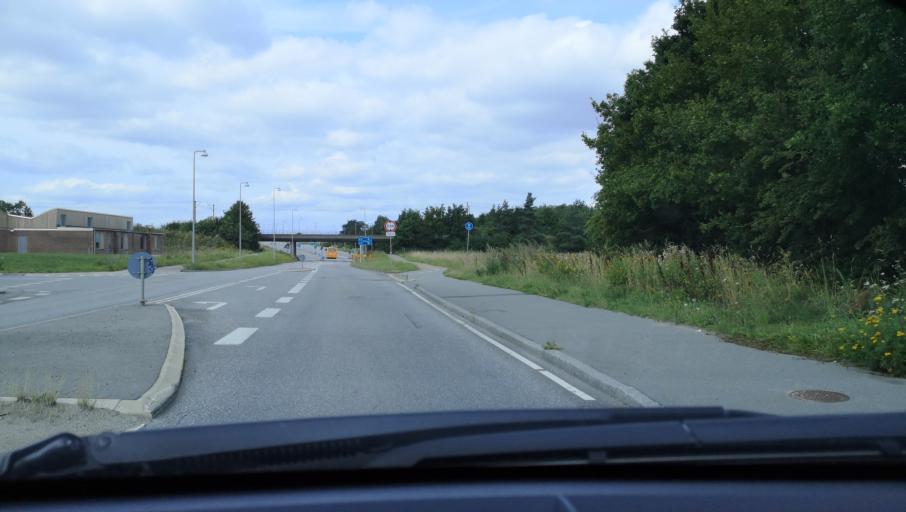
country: DK
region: Zealand
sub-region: Solrod Kommune
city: Solrod
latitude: 55.5029
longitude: 12.1840
